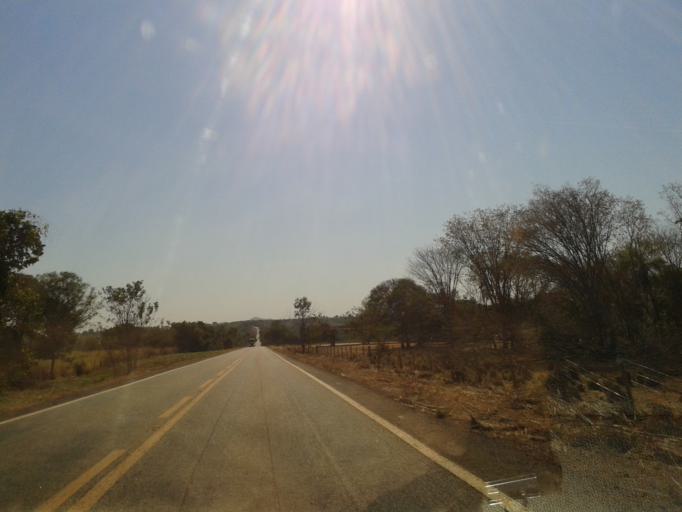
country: BR
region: Goias
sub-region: Crixas
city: Crixas
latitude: -14.1915
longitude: -50.3824
